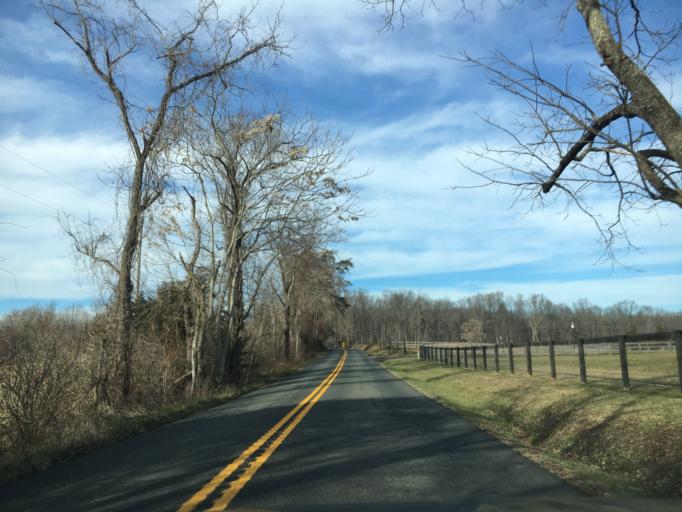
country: US
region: Virginia
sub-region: Fauquier County
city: Marshall
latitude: 38.7975
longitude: -77.9926
